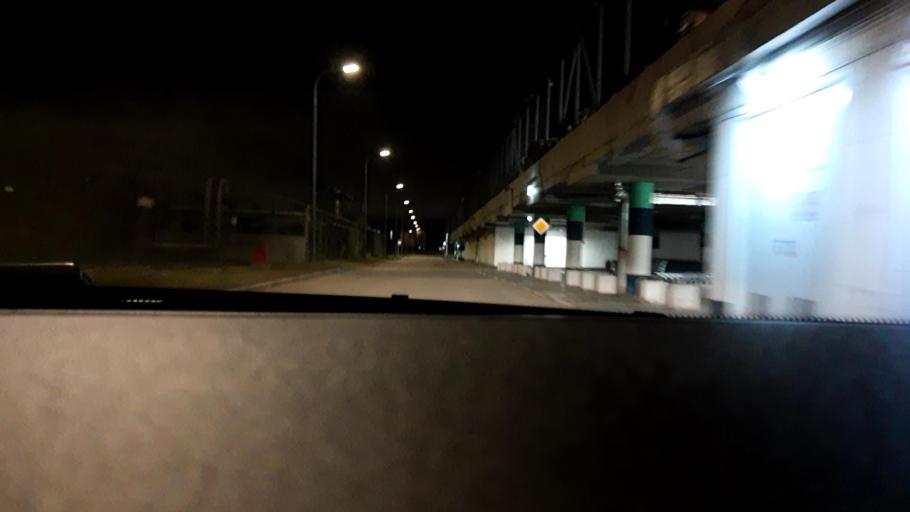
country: RU
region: Nizjnij Novgorod
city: Afonino
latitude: 56.2246
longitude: 44.0685
